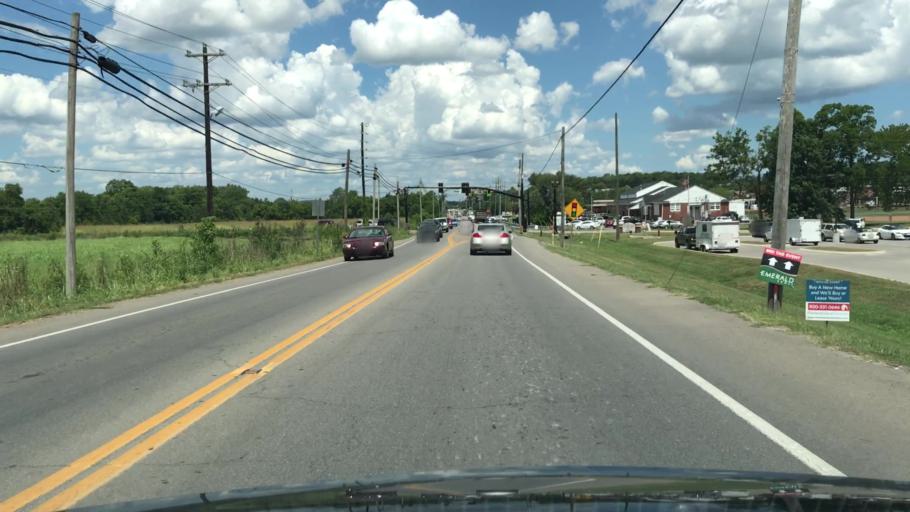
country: US
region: Tennessee
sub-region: Williamson County
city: Nolensville
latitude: 35.9578
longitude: -86.6722
